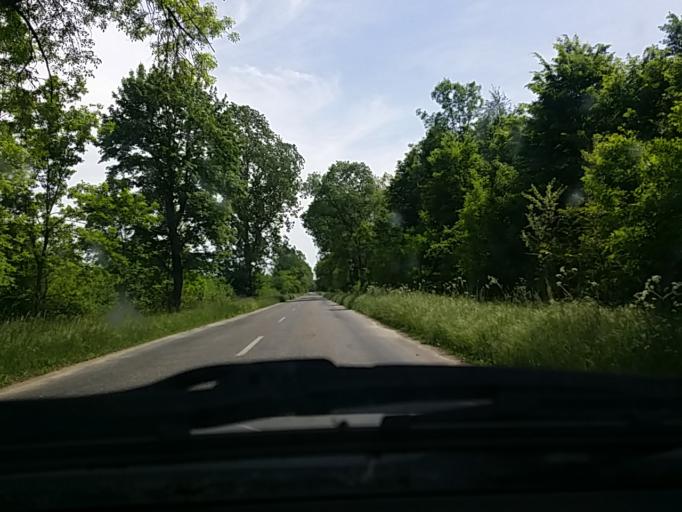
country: HU
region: Baranya
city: Sellye
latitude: 45.9066
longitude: 17.6800
